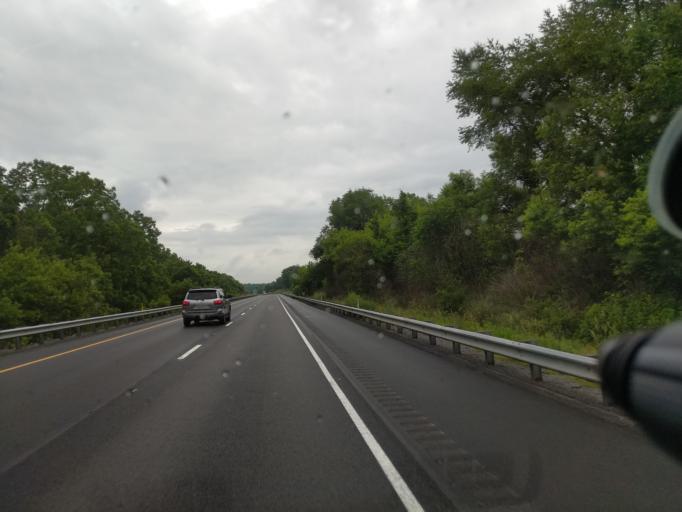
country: US
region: Pennsylvania
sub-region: Northumberland County
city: Milton
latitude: 41.0450
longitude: -76.8195
